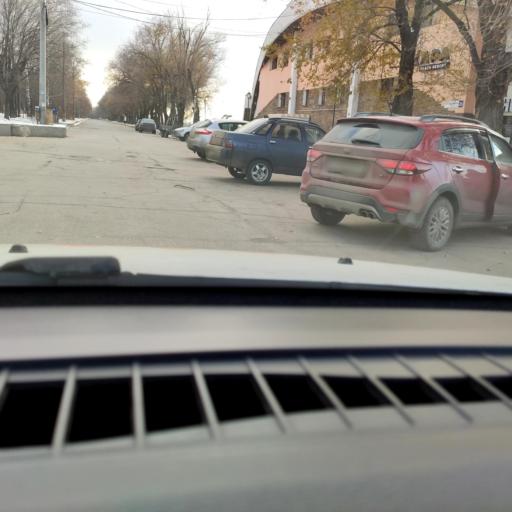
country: RU
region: Samara
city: Tol'yatti
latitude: 53.5016
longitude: 49.2530
